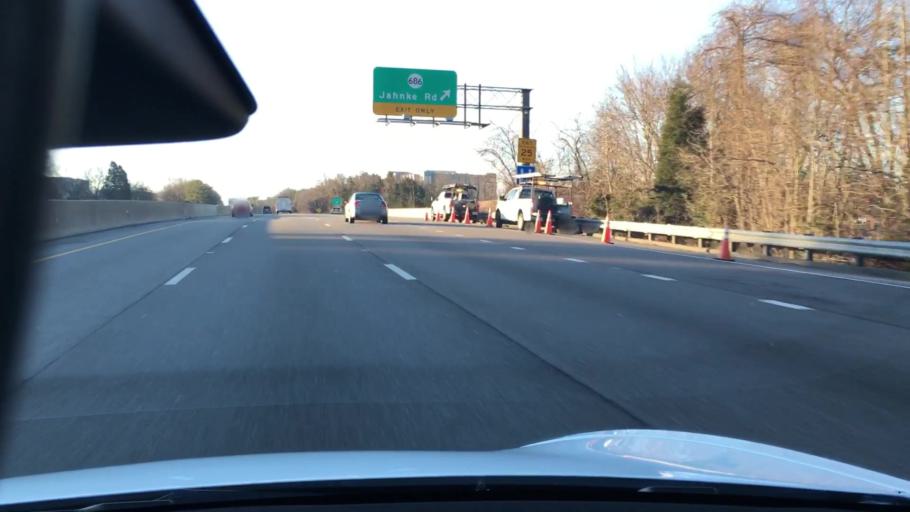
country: US
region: Virginia
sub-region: Chesterfield County
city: Bon Air
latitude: 37.5169
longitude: -77.5284
